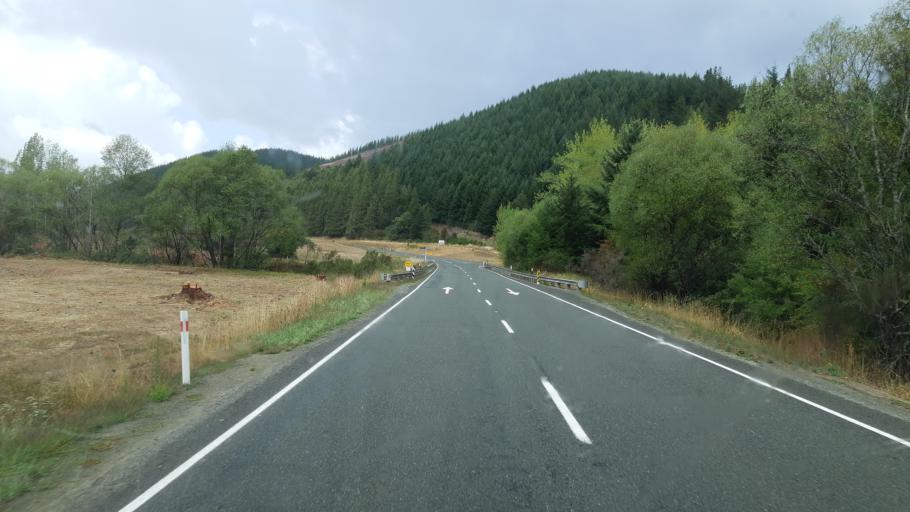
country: NZ
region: Tasman
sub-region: Tasman District
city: Wakefield
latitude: -41.4722
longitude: 172.8434
